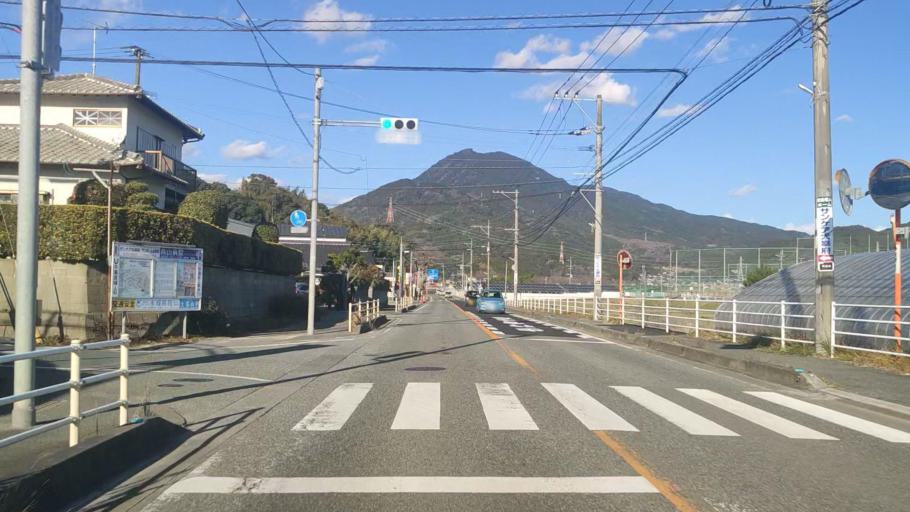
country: JP
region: Fukuoka
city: Dazaifu
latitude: 33.5019
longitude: 130.5500
